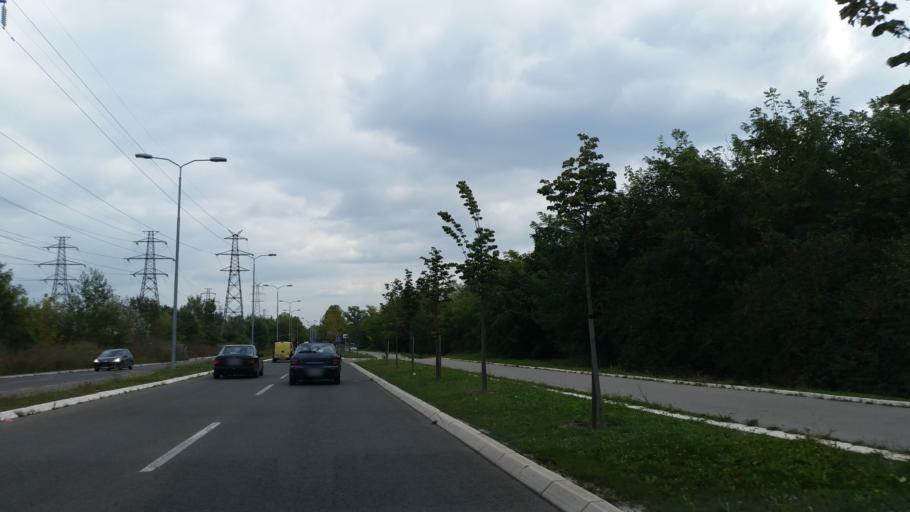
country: RS
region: Central Serbia
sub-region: Belgrade
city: Zemun
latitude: 44.8216
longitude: 20.3701
